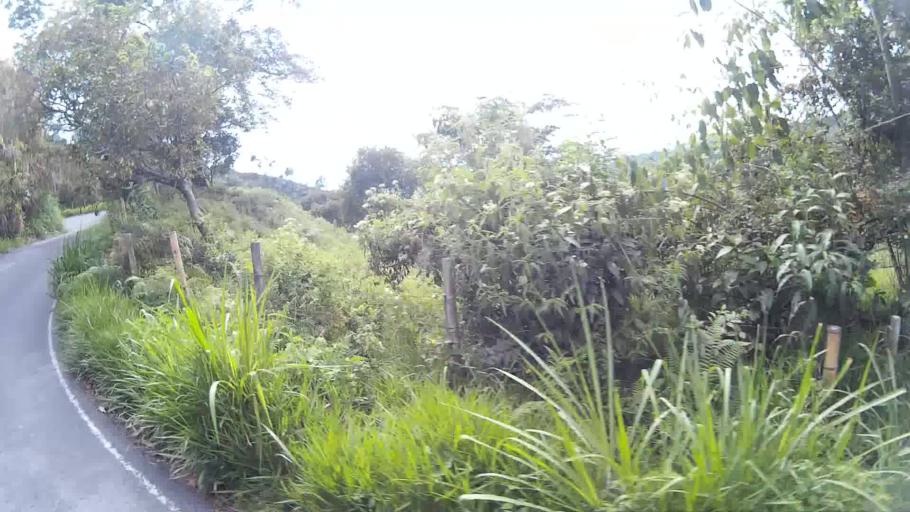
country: CO
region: Risaralda
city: Marsella
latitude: 4.9013
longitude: -75.7361
